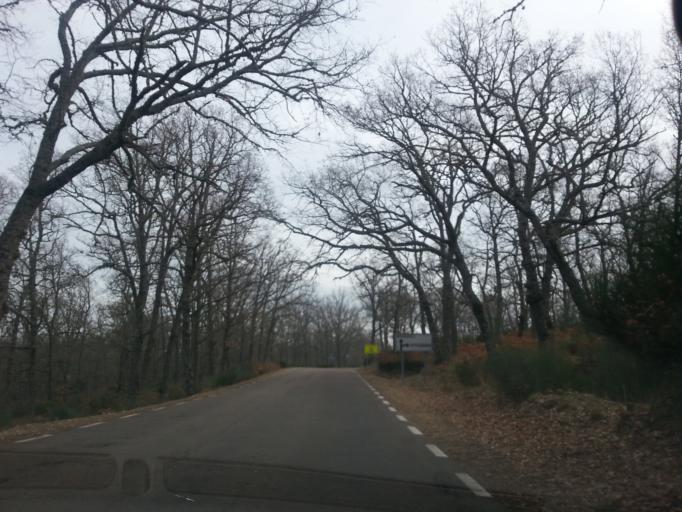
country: ES
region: Castille and Leon
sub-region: Provincia de Salamanca
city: La Alberca
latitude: 40.4894
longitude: -6.0952
